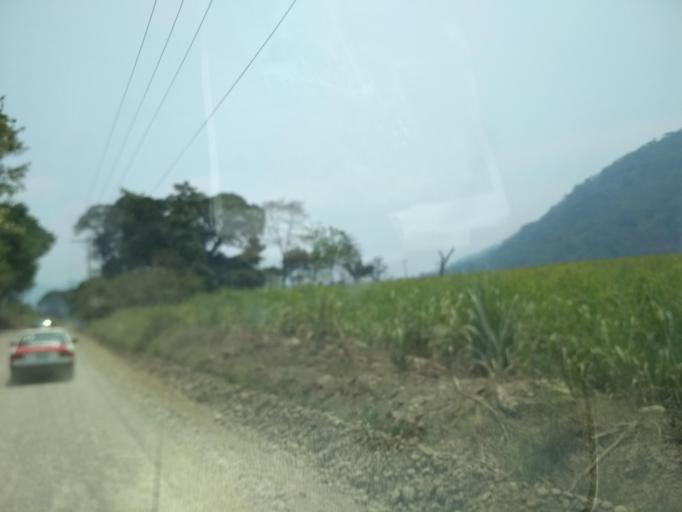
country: MX
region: Veracruz
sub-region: Tezonapa
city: Laguna Chica (Pueblo Nuevo)
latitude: 18.5635
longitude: -96.7226
